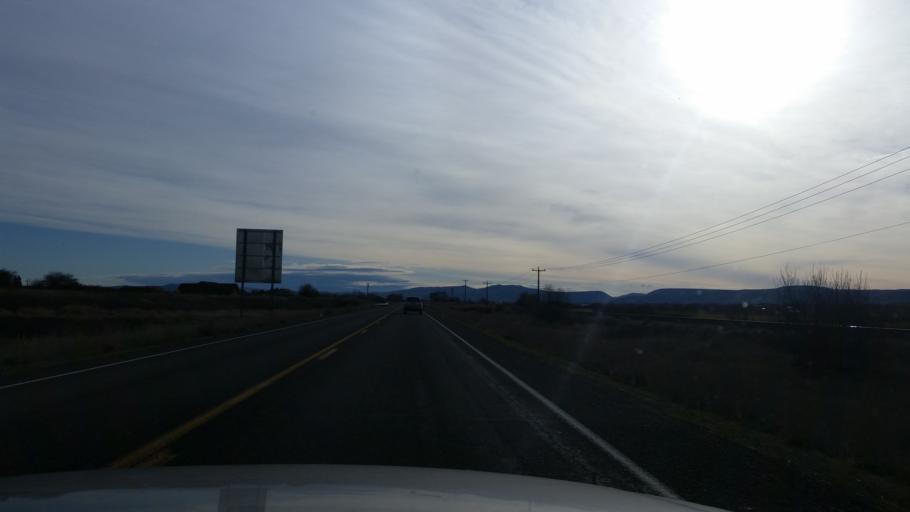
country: US
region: Washington
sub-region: Kittitas County
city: Ellensburg
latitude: 47.0339
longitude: -120.6099
